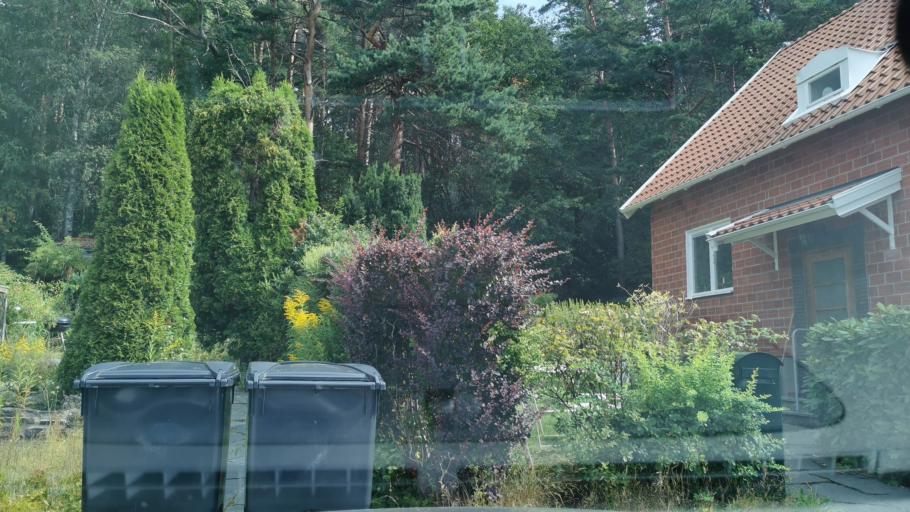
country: SE
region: Vaestra Goetaland
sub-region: Molndal
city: Moelndal
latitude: 57.6661
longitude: 11.9956
